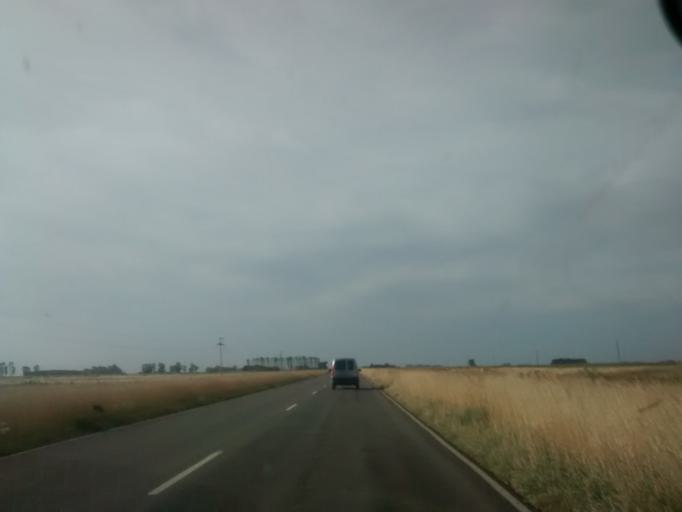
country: AR
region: Buenos Aires
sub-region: Partido de Ayacucho
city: Ayacucho
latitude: -36.9053
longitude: -58.5282
